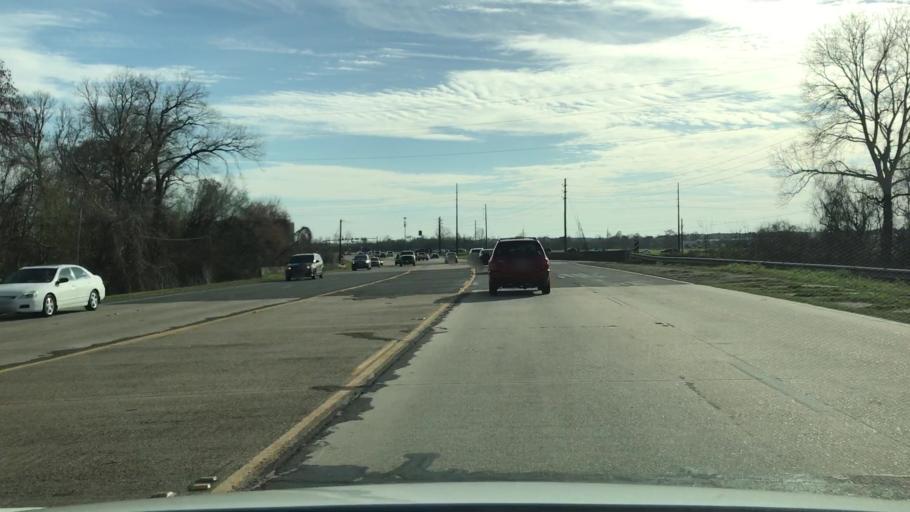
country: US
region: Louisiana
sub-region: Bossier Parish
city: Bossier City
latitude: 32.4412
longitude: -93.7051
